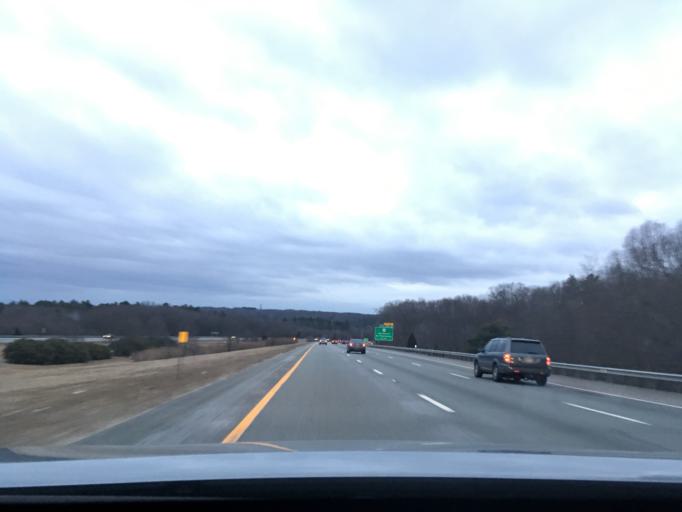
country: US
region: Rhode Island
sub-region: Providence County
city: Greenville
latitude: 41.8816
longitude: -71.5175
